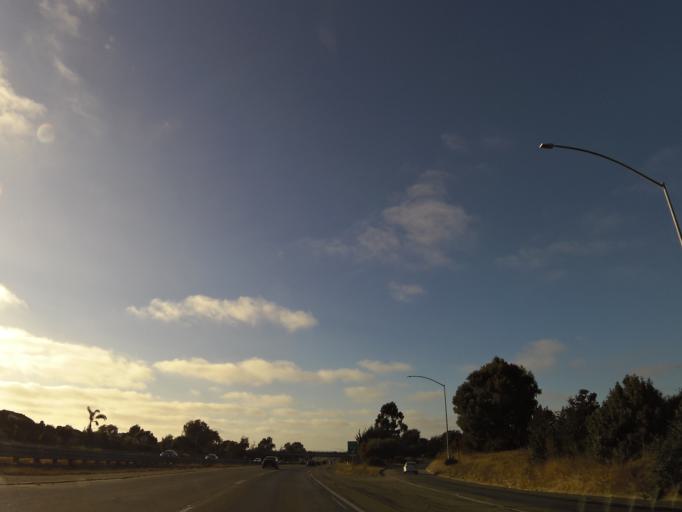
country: US
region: California
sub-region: Monterey County
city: Boronda
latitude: 36.6948
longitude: -121.6629
